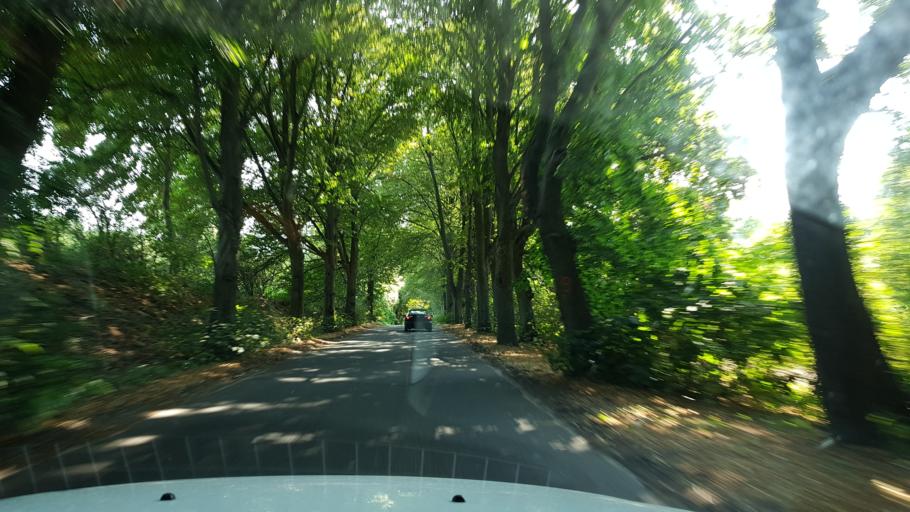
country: PL
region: West Pomeranian Voivodeship
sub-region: Powiat gryfinski
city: Chojna
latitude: 52.9537
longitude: 14.5010
